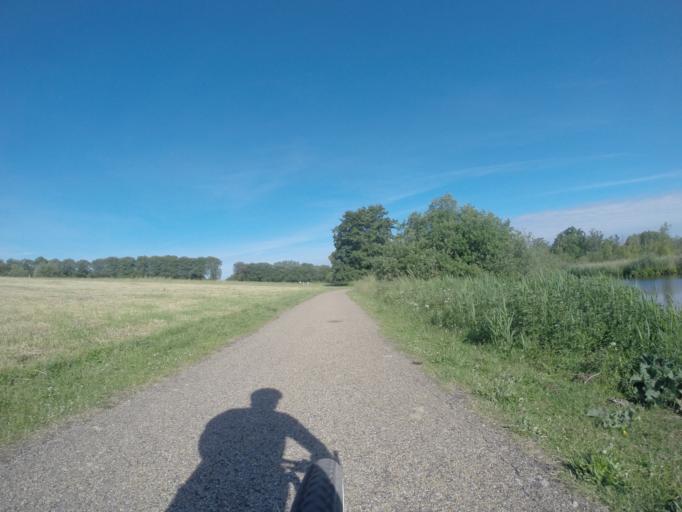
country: DK
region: Capital Region
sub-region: Herlev Kommune
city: Herlev
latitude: 55.7482
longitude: 12.4409
